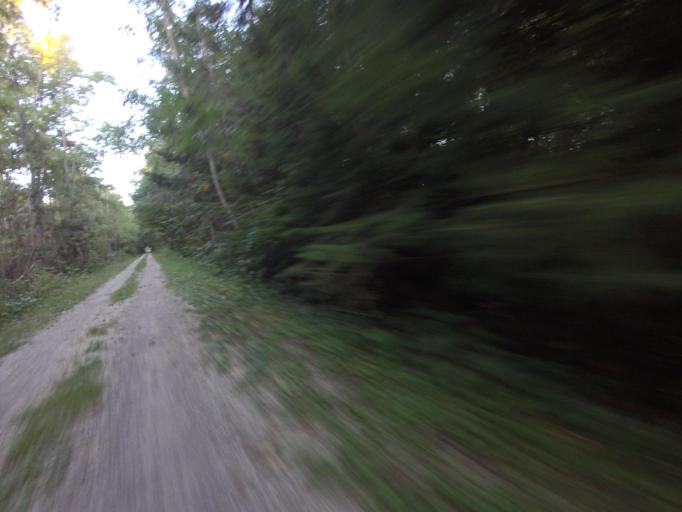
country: CA
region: Ontario
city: Goderich
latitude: 43.7520
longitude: -81.6640
